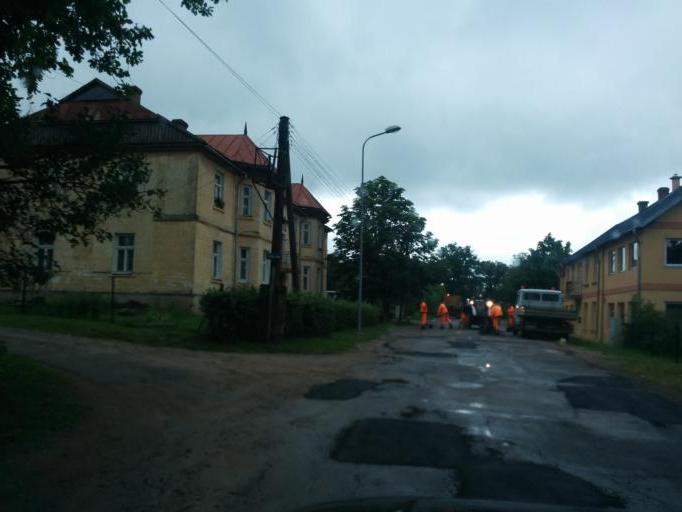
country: LV
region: Smiltene
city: Smiltene
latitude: 57.4259
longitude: 25.8941
